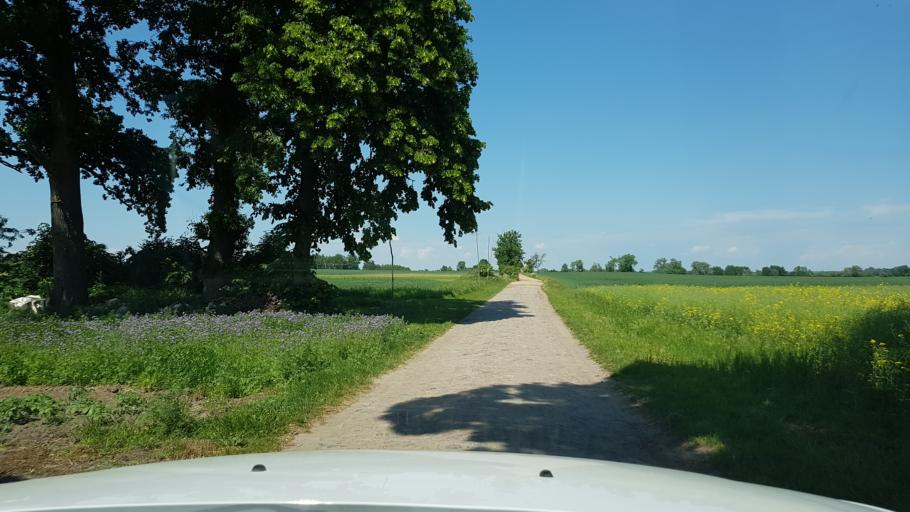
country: PL
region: West Pomeranian Voivodeship
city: Trzcinsko Zdroj
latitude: 52.9448
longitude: 14.5808
